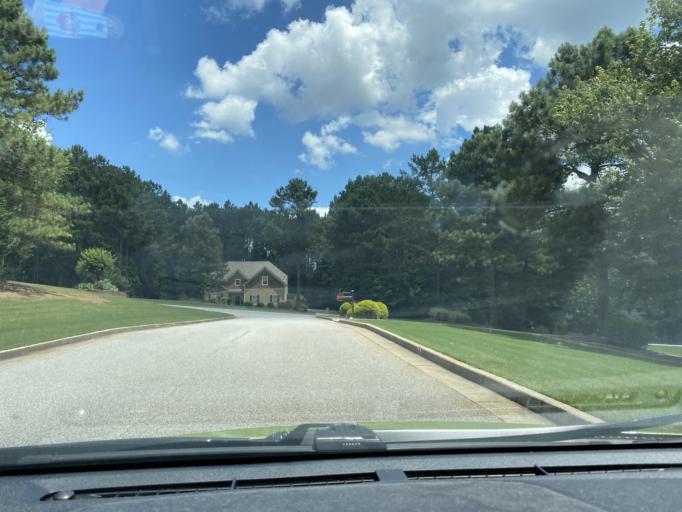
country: US
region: Georgia
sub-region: Fulton County
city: Palmetto
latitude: 33.4322
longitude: -84.6757
